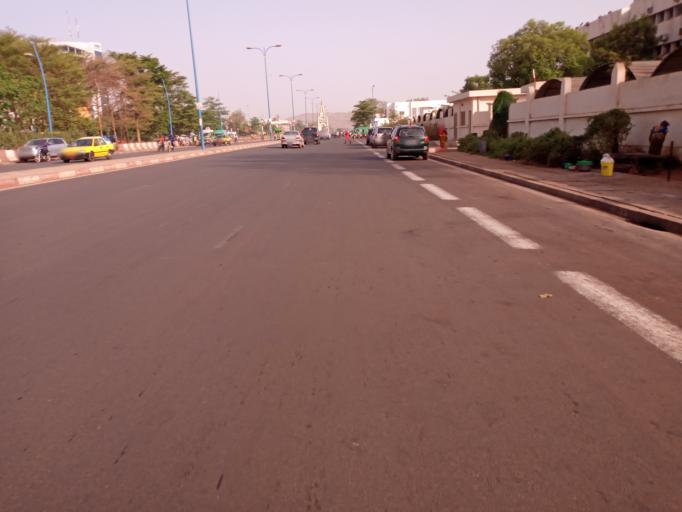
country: ML
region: Bamako
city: Bamako
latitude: 12.6345
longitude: -8.0030
